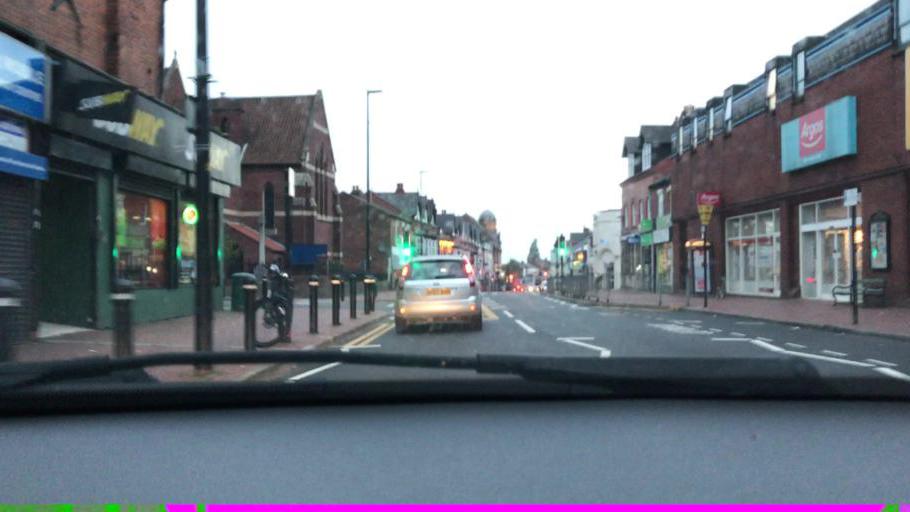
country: GB
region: England
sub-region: Sandwell
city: Smethwick
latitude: 52.4750
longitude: -1.9695
